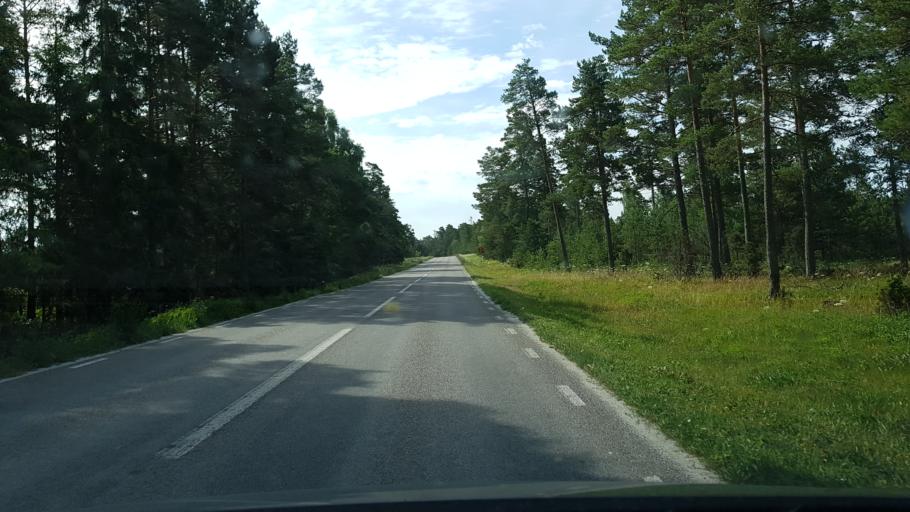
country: SE
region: Gotland
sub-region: Gotland
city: Hemse
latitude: 57.4635
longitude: 18.5716
